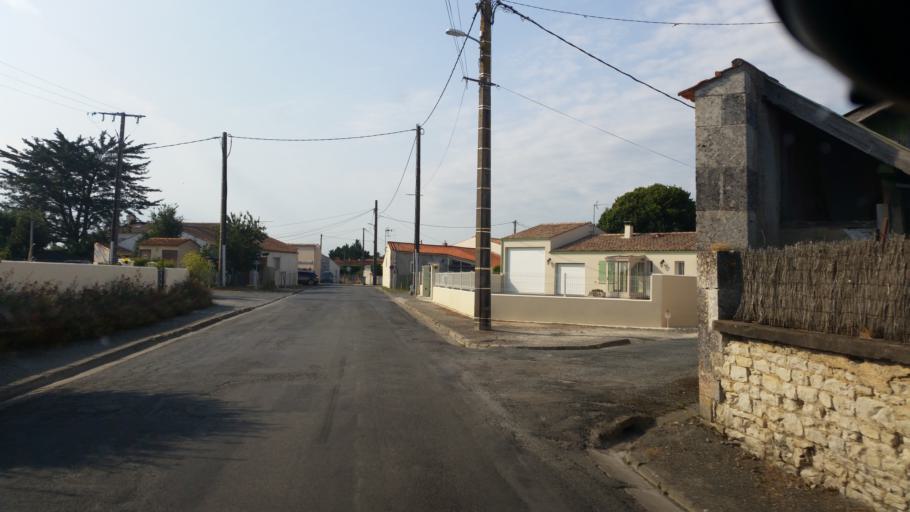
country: FR
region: Poitou-Charentes
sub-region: Departement de la Charente-Maritime
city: Saint-Jean-de-Liversay
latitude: 46.3015
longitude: -0.8939
